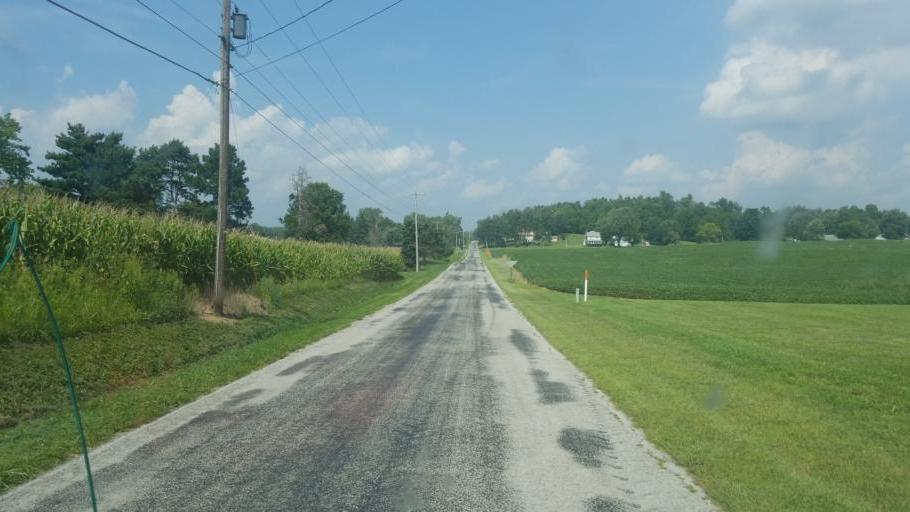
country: US
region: Ohio
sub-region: Richland County
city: Shelby
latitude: 40.8819
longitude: -82.5956
